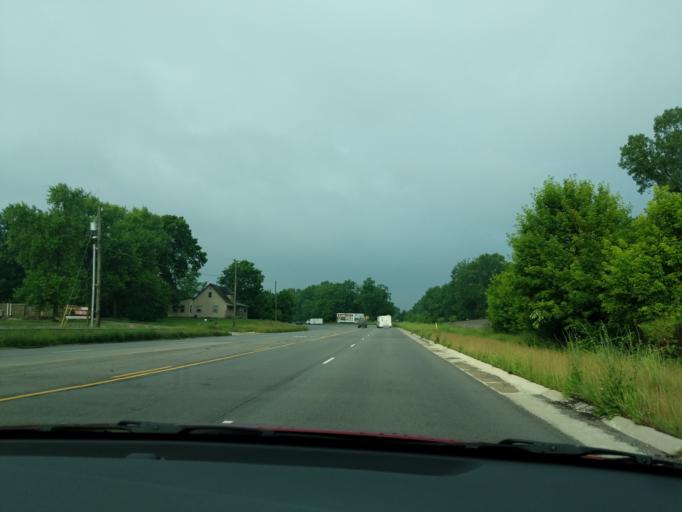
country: US
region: Indiana
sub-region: Hancock County
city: McCordsville
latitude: 39.8821
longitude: -85.9475
